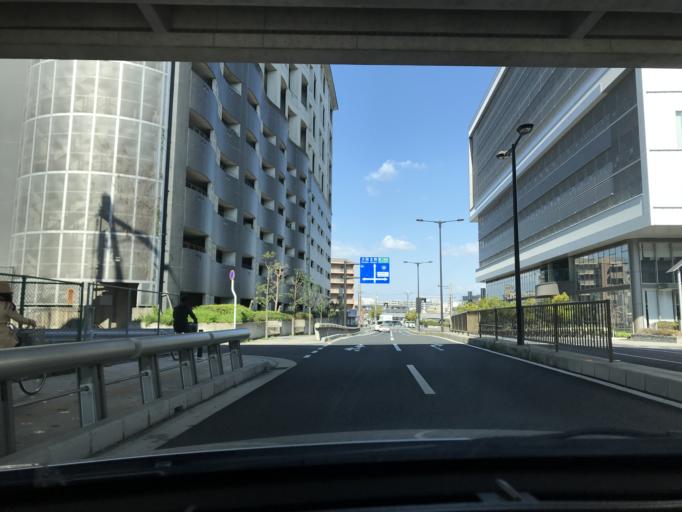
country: JP
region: Nara
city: Nara-shi
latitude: 34.6786
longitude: 135.8180
